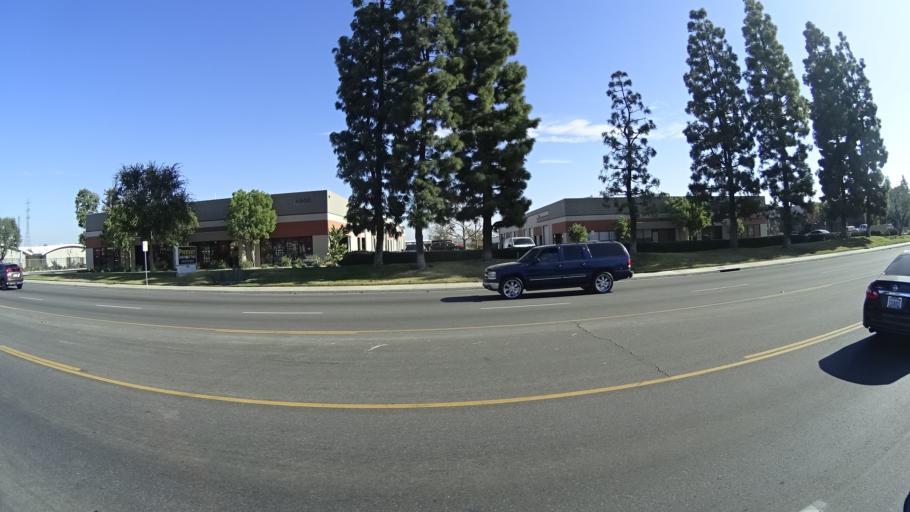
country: US
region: California
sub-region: Kern County
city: Greenacres
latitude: 35.3148
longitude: -119.0746
